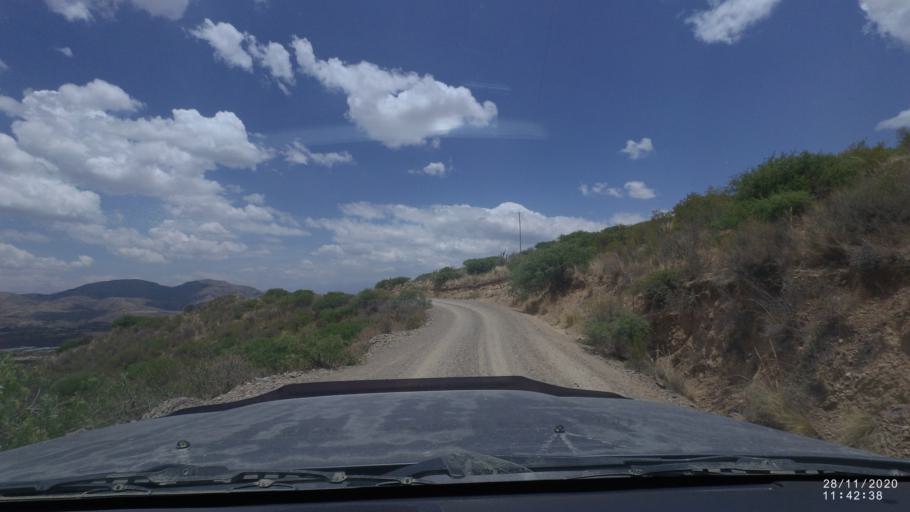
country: BO
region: Cochabamba
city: Tarata
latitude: -17.6635
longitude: -66.0465
